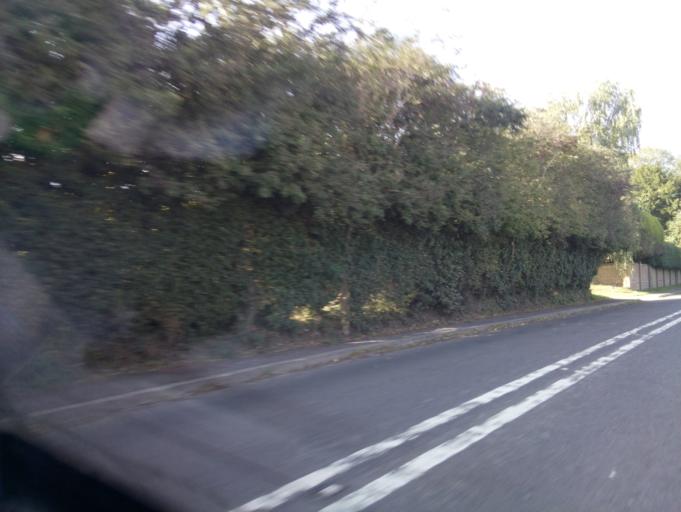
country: GB
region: England
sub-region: Hampshire
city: Alton
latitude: 51.1122
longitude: -0.9942
